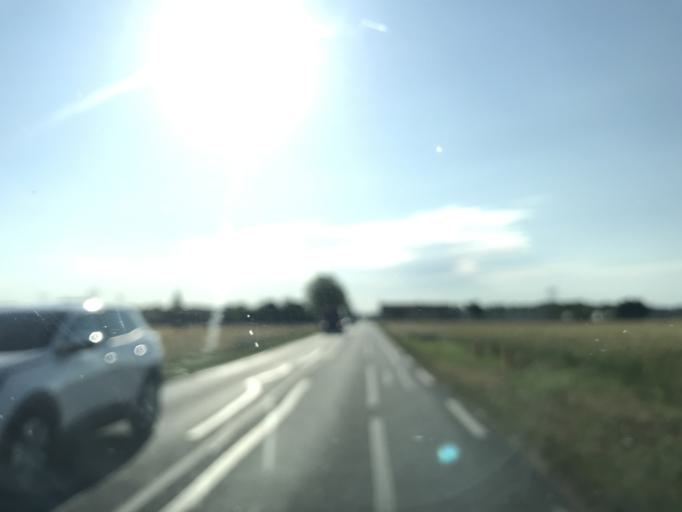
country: FR
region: Rhone-Alpes
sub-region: Departement du Rhone
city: Mions
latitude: 45.6526
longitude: 4.9452
